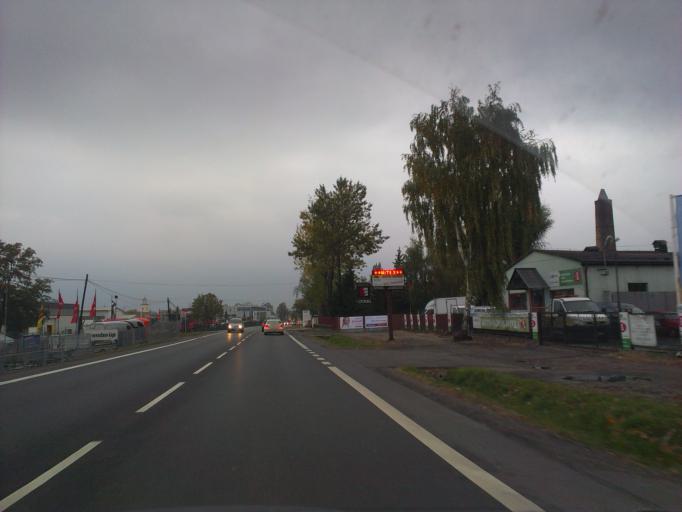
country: PL
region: Greater Poland Voivodeship
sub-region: Powiat poznanski
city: Zlotniki
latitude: 52.4835
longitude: 16.8587
